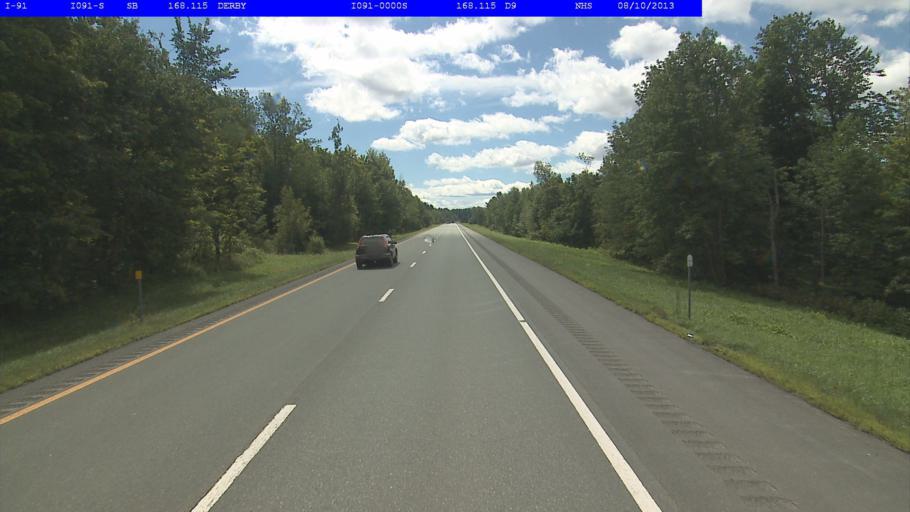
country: US
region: Vermont
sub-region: Orleans County
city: Newport
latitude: 44.8956
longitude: -72.1752
